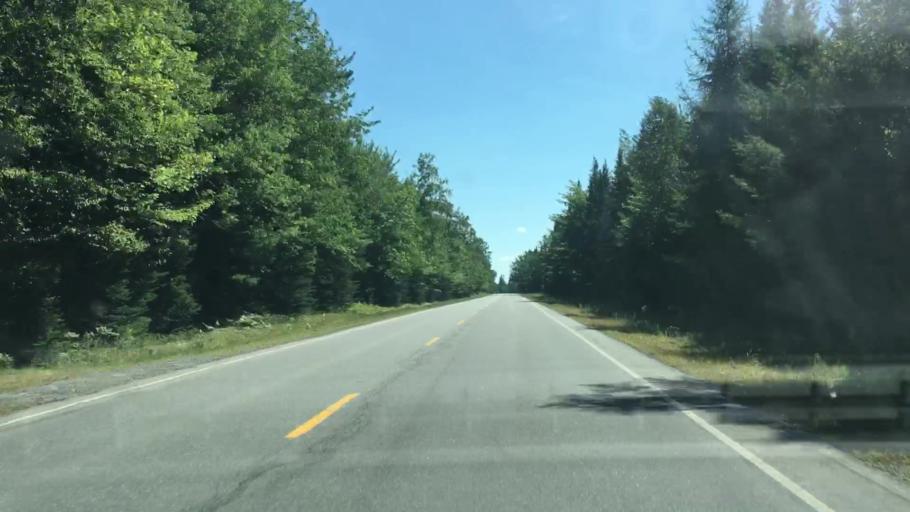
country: US
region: Maine
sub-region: Piscataquis County
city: Milo
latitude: 45.2062
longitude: -68.9088
